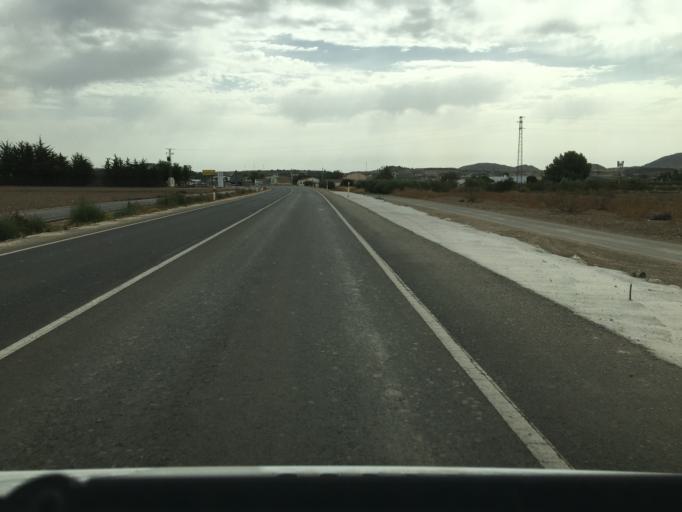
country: ES
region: Andalusia
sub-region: Provincia de Almeria
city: Huercal-Overa
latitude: 37.4148
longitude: -1.8962
